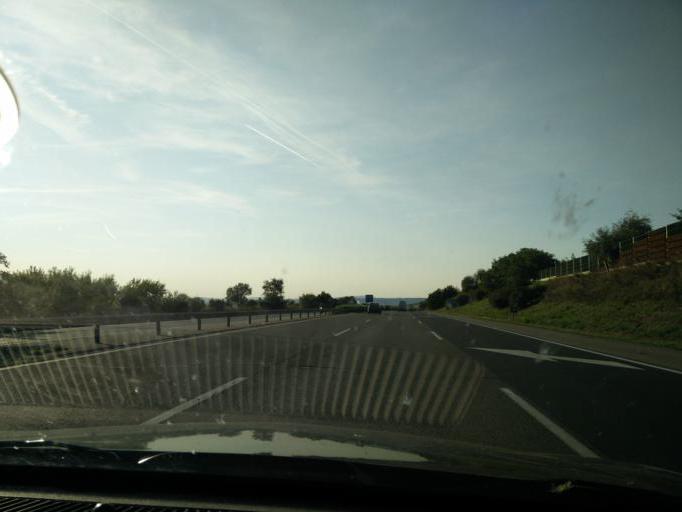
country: HU
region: Pest
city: Biatorbagy
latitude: 47.4799
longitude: 18.8439
